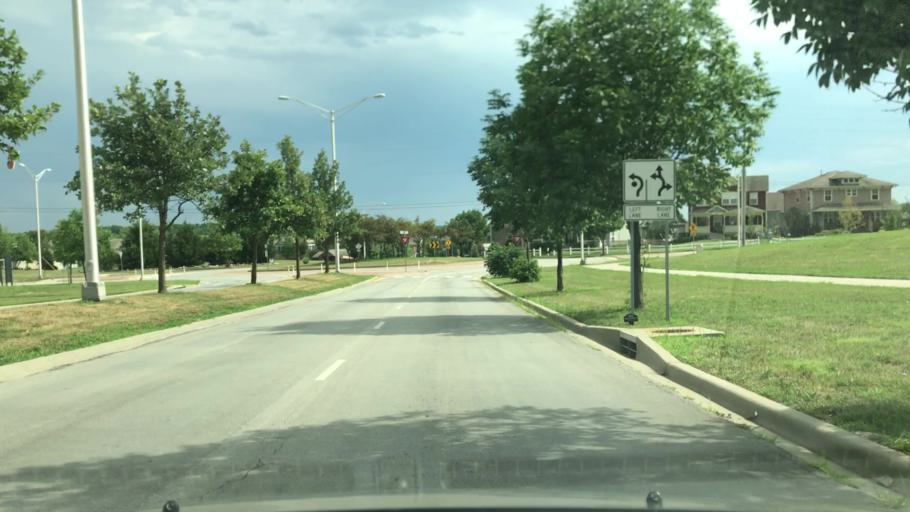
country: US
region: Missouri
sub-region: Jackson County
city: Lees Summit
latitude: 38.9067
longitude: -94.4472
